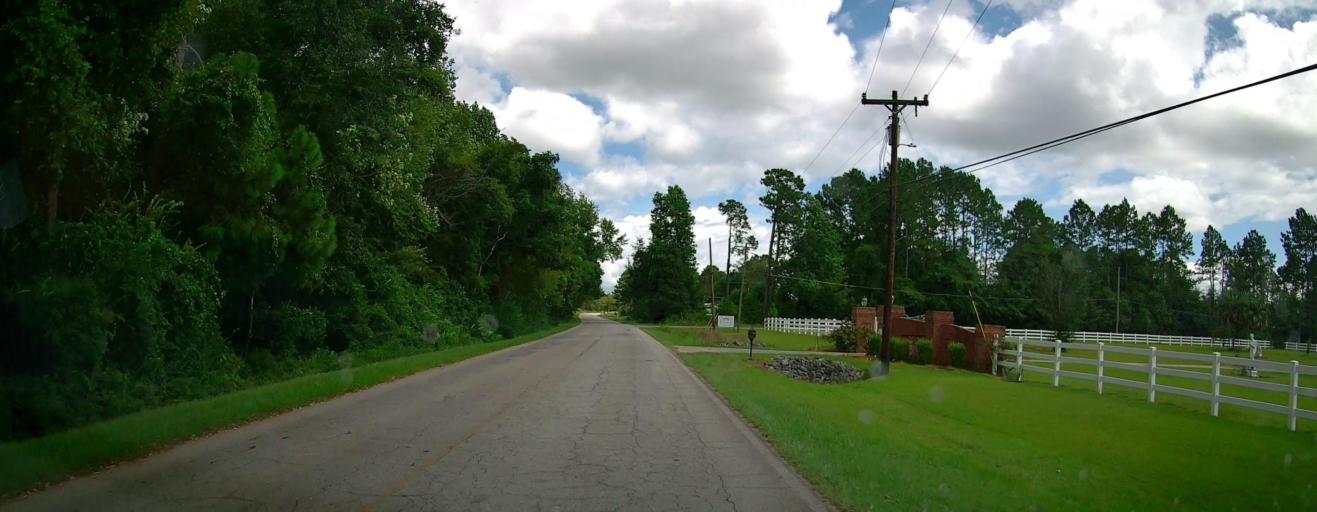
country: US
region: Georgia
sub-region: Ben Hill County
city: Fitzgerald
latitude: 31.7029
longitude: -83.2265
